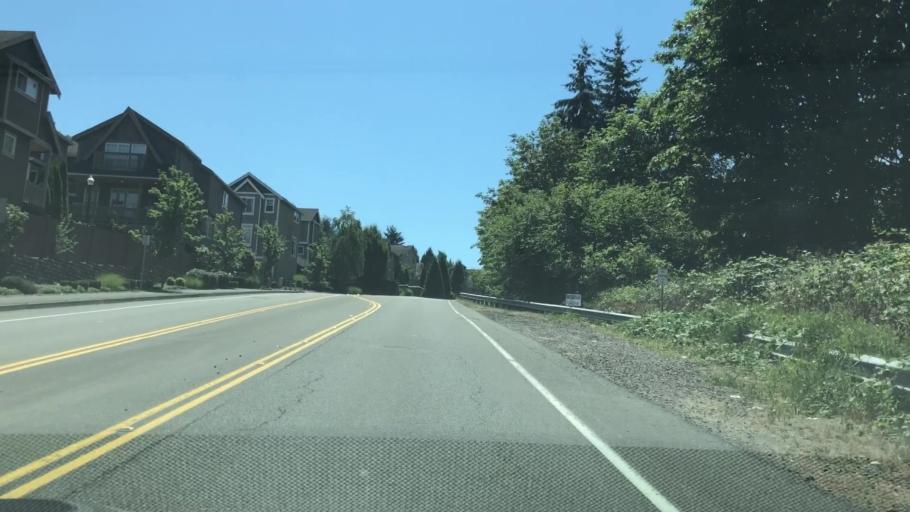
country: US
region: Washington
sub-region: King County
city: Woodinville
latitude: 47.7523
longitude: -122.1744
